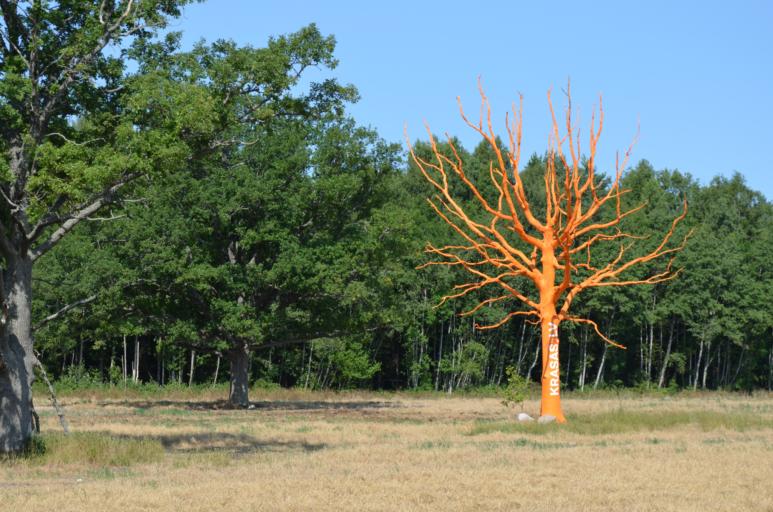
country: LV
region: Salacgrivas
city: Salacgriva
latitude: 57.6816
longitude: 24.3825
